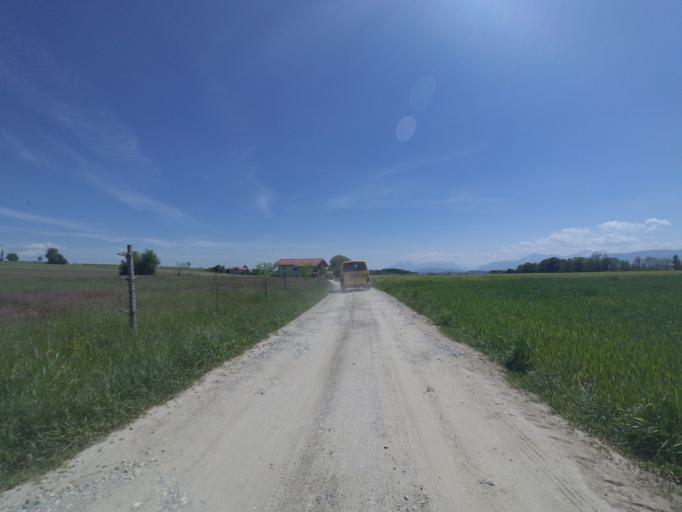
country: DE
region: Bavaria
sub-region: Upper Bavaria
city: Petting
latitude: 47.9403
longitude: 12.7968
